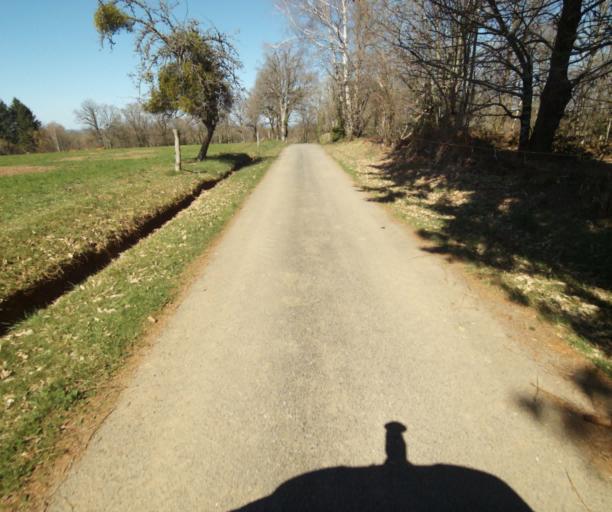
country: FR
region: Limousin
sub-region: Departement de la Correze
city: Chamboulive
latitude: 45.3996
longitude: 1.6805
